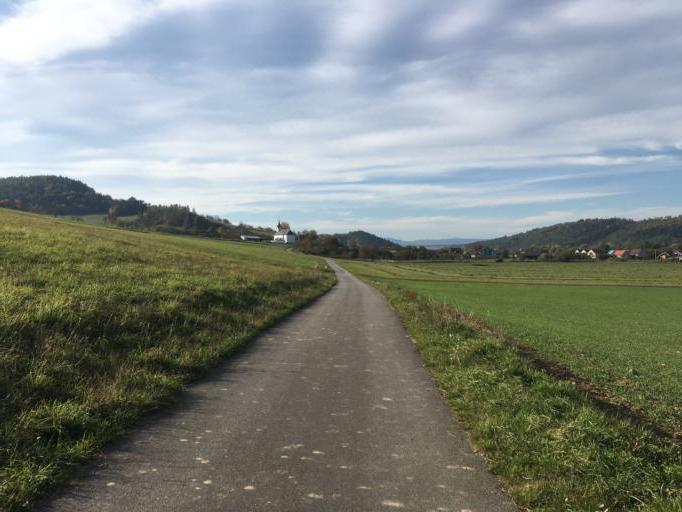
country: SK
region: Trenciansky
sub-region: Okres Povazska Bystrica
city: Povazska Bystrica
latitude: 49.0478
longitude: 18.4157
